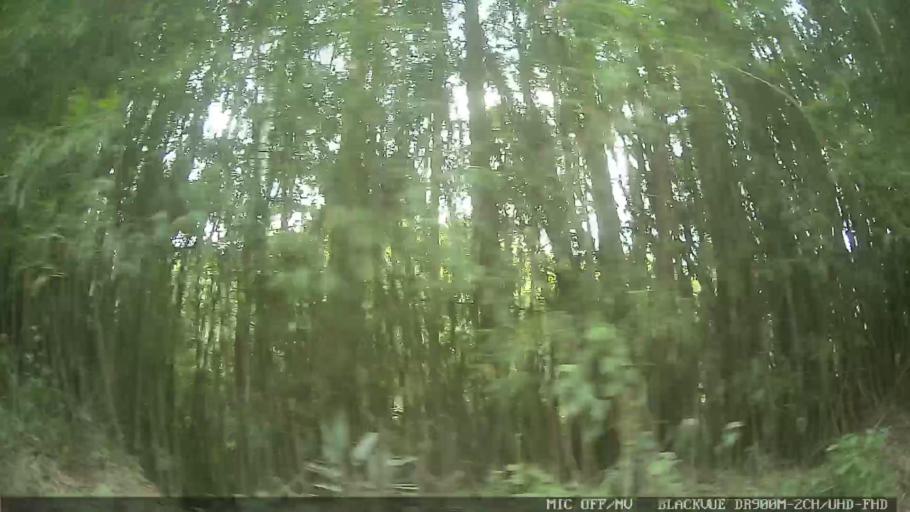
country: BR
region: Sao Paulo
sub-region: Atibaia
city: Atibaia
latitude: -23.1526
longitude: -46.5161
